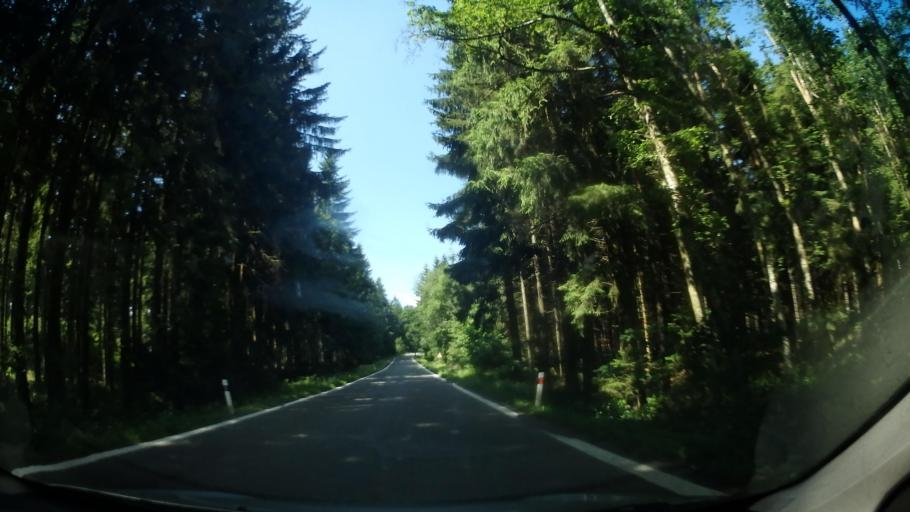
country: CZ
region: Vysocina
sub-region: Okres Zd'ar nad Sazavou
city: Nove Mesto na Morave
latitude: 49.6112
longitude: 16.0198
